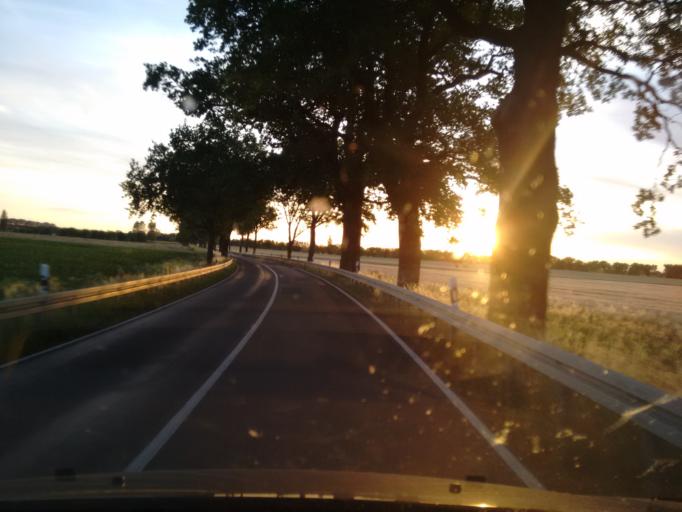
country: DE
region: Brandenburg
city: Beeskow
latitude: 52.1610
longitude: 14.2922
